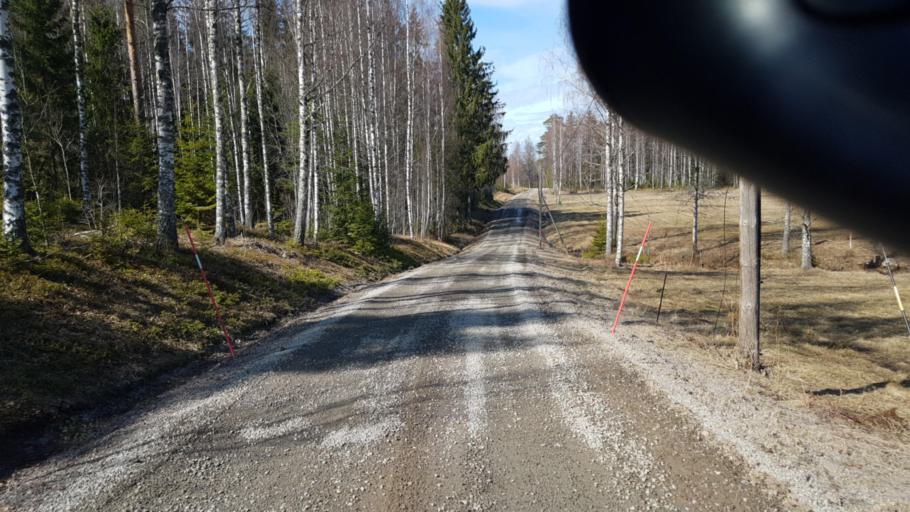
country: SE
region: Vaermland
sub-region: Arvika Kommun
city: Arvika
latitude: 59.5721
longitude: 12.8334
